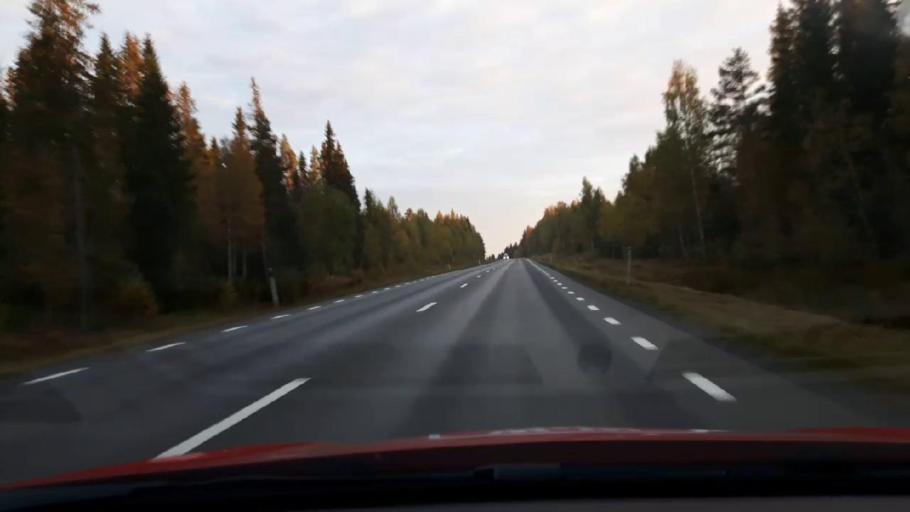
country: SE
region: Jaemtland
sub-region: OEstersunds Kommun
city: Lit
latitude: 63.3051
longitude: 14.8704
